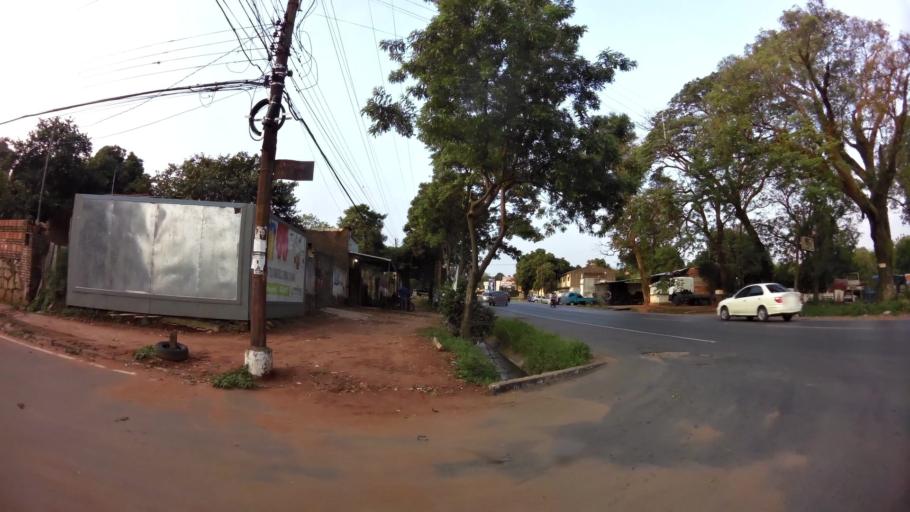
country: PY
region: Central
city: Villa Elisa
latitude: -25.3532
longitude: -57.5931
